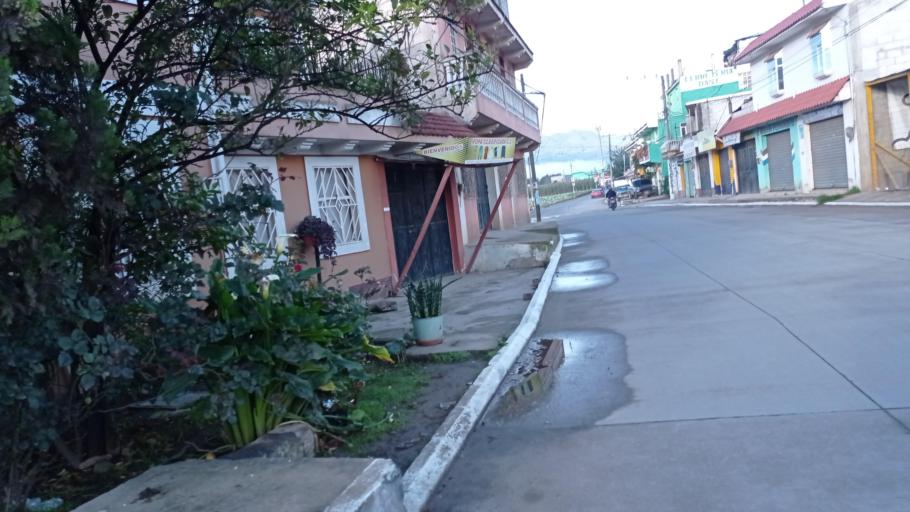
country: GT
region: Quetzaltenango
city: Olintepeque
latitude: 14.8662
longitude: -91.5105
